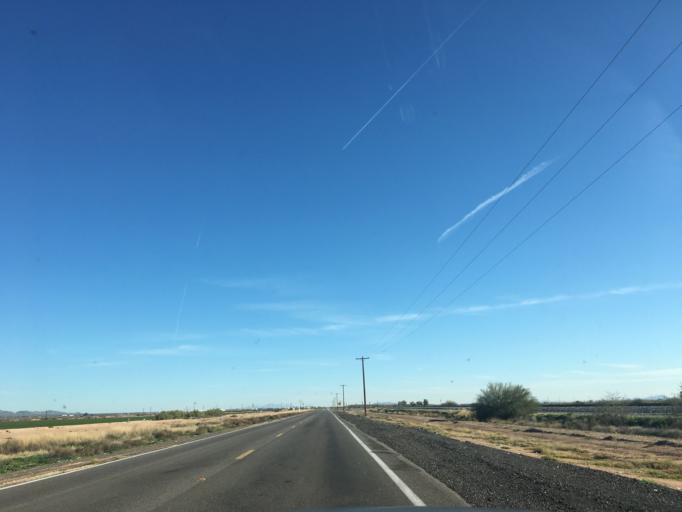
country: US
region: Arizona
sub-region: Pinal County
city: Maricopa
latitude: 33.0088
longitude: -111.9703
